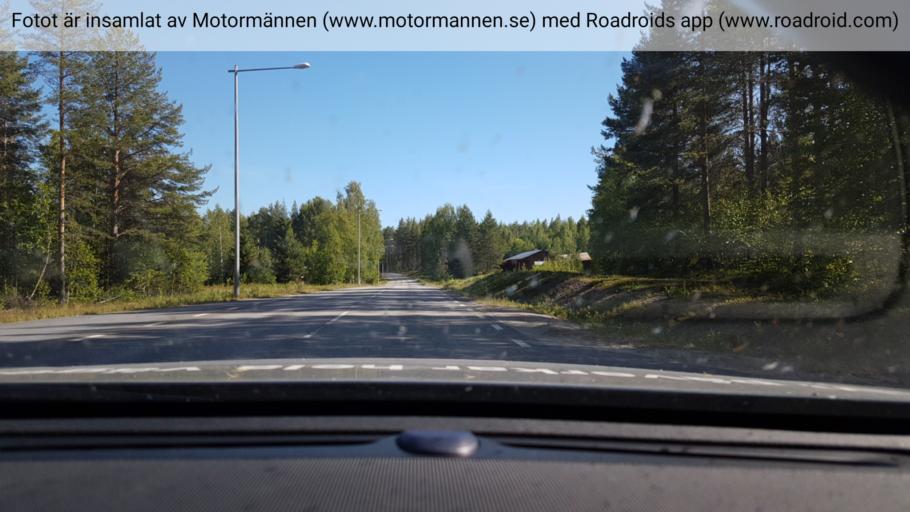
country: SE
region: Vaesterbotten
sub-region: Lycksele Kommun
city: Lycksele
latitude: 64.6168
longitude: 18.6400
